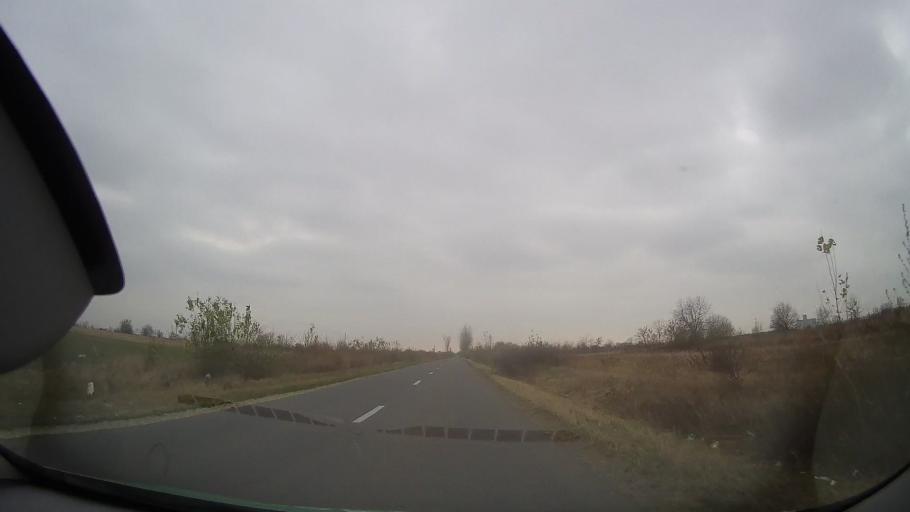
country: RO
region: Ialomita
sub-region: Comuna Manasia
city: Manasia
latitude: 44.7182
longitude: 26.6837
